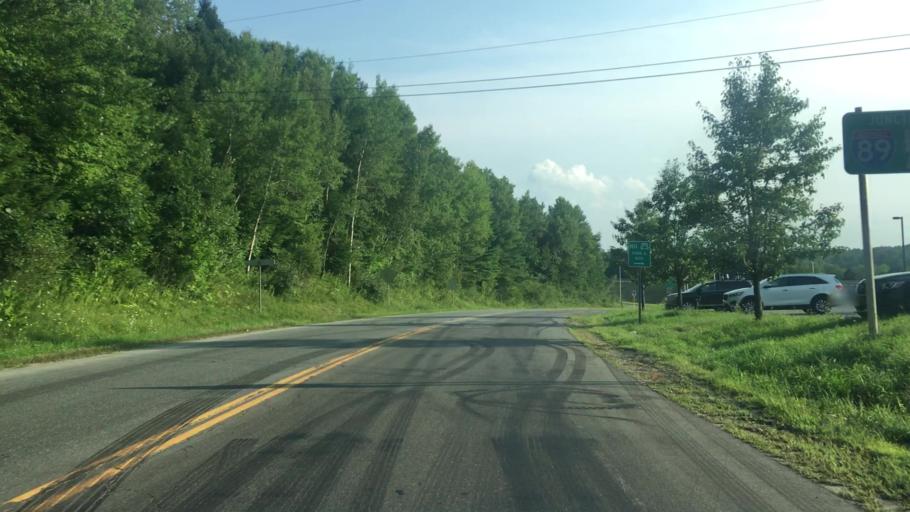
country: US
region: New Hampshire
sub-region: Sullivan County
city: Grantham
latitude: 43.5008
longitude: -72.1308
